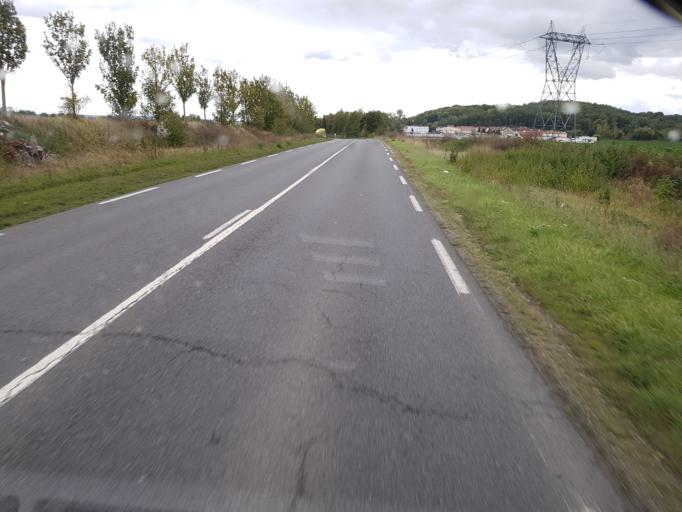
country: FR
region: Ile-de-France
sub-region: Departement de Seine-et-Marne
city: Monthyon
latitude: 48.9979
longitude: 2.8506
